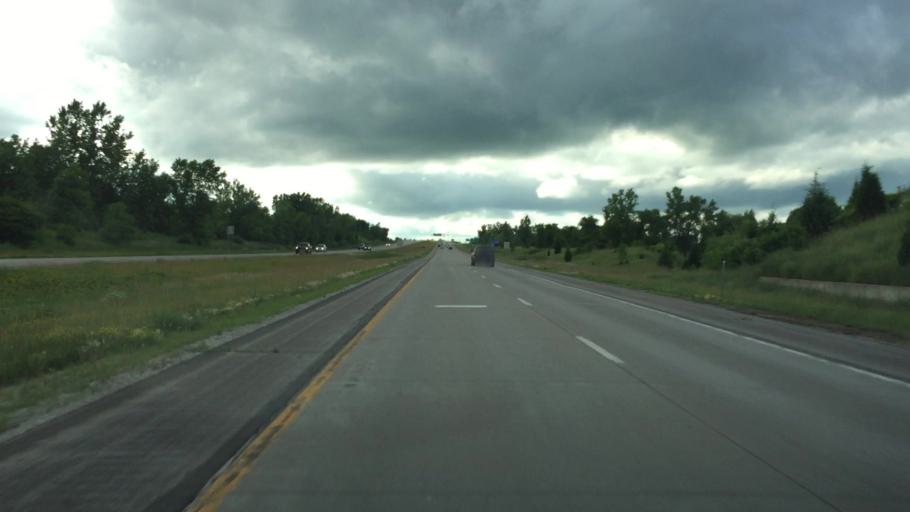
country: US
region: Iowa
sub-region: Polk County
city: Altoona
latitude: 41.6337
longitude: -93.5035
